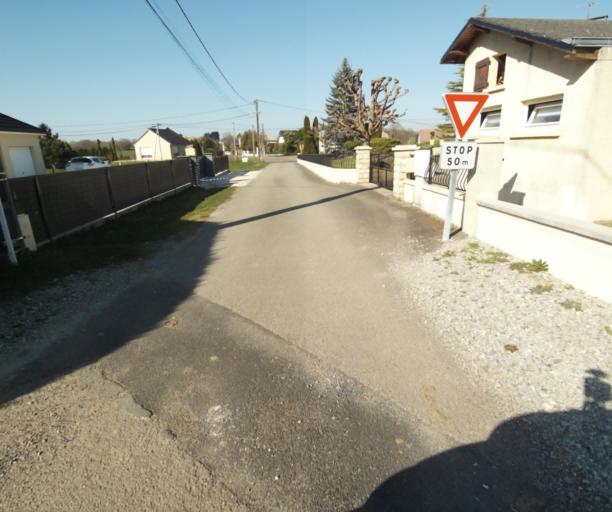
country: FR
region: Limousin
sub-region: Departement de la Correze
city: Saint-Mexant
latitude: 45.2954
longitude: 1.6906
